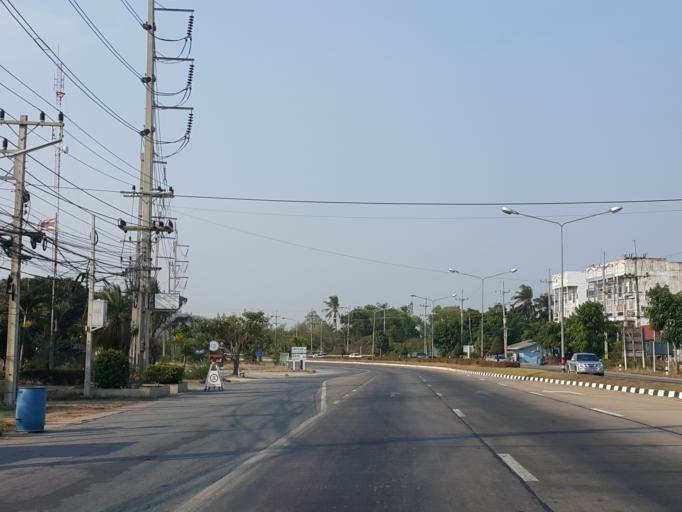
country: TH
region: Suphan Buri
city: Doembang Nangbuat
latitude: 14.8099
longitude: 100.1180
